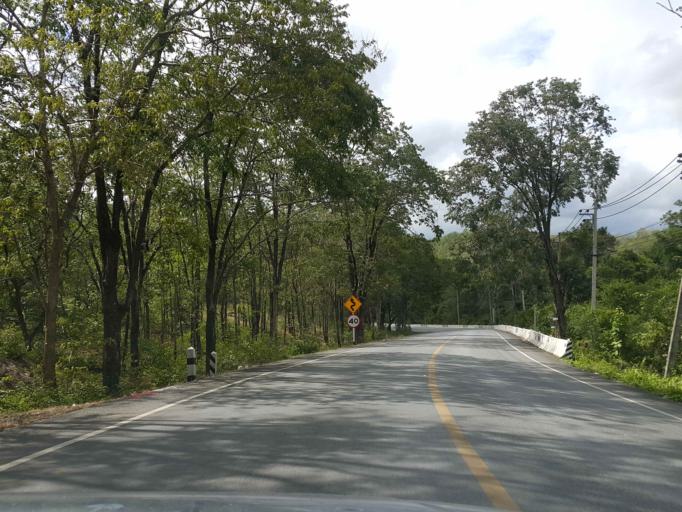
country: TH
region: Tak
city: Tak
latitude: 16.8044
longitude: 98.9971
